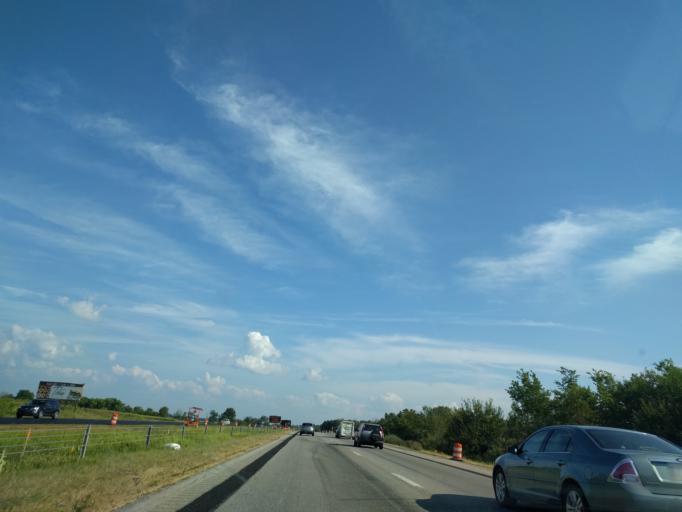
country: US
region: Indiana
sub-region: Boone County
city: Thorntown
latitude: 40.1913
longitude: -86.5684
